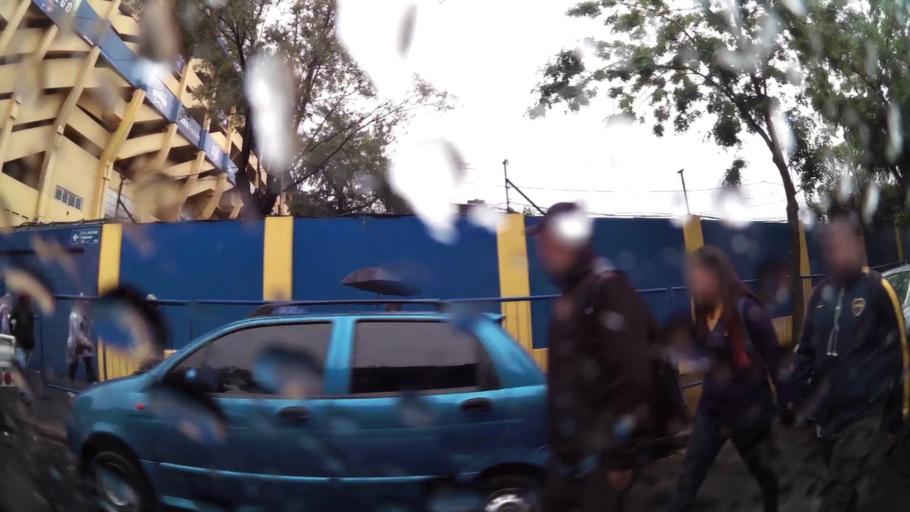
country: AR
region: Buenos Aires F.D.
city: Buenos Aires
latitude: -34.6344
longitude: -58.3648
